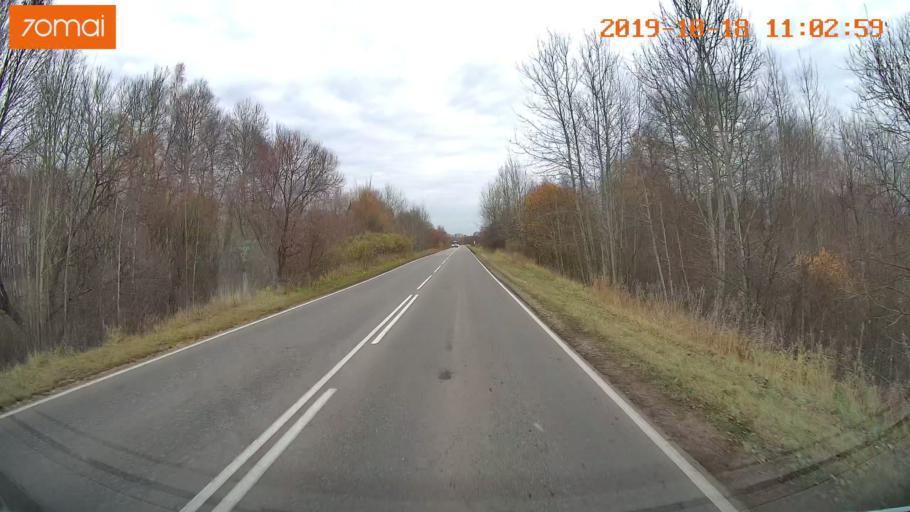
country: RU
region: Tula
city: Yepifan'
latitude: 53.8733
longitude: 38.5451
